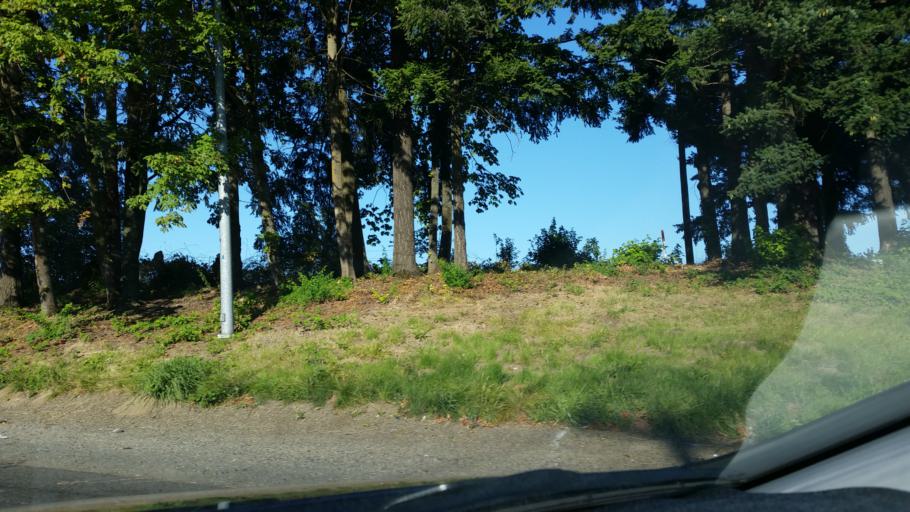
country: US
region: Oregon
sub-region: Marion County
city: Hubbard
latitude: 45.2345
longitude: -122.8063
